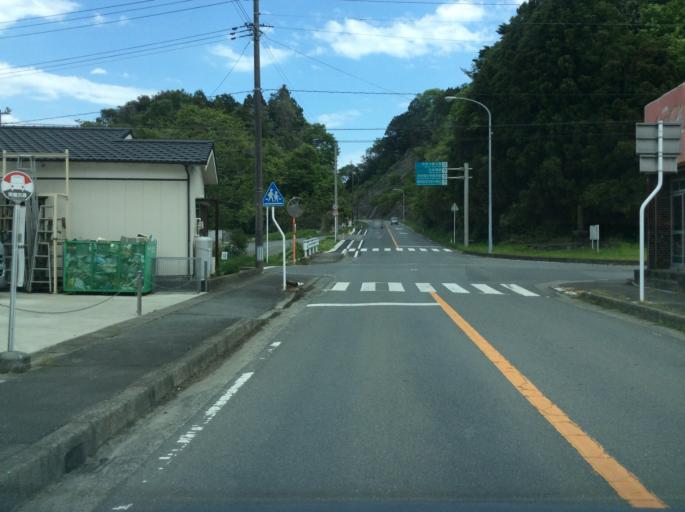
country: JP
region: Ibaraki
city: Kitaibaraki
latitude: 36.8793
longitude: 140.7848
